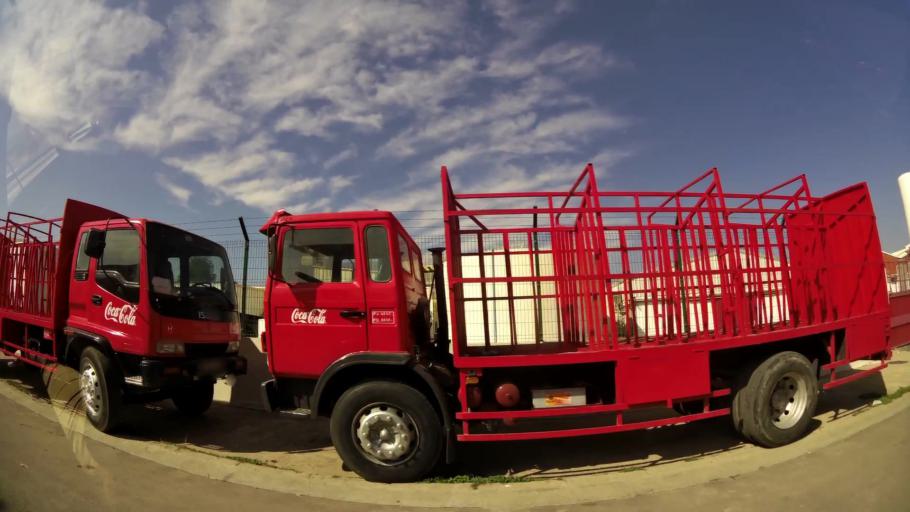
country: MA
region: Oriental
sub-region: Oujda-Angad
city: Oujda
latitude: 34.7049
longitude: -1.8911
